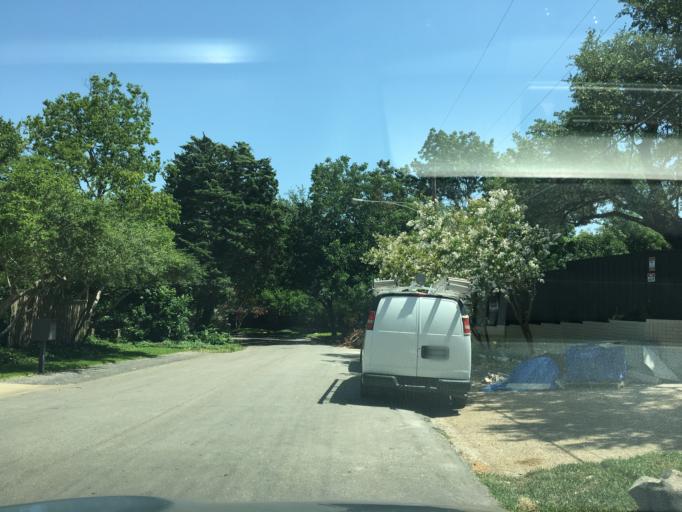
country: US
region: Texas
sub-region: Dallas County
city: University Park
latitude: 32.9076
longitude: -96.7823
